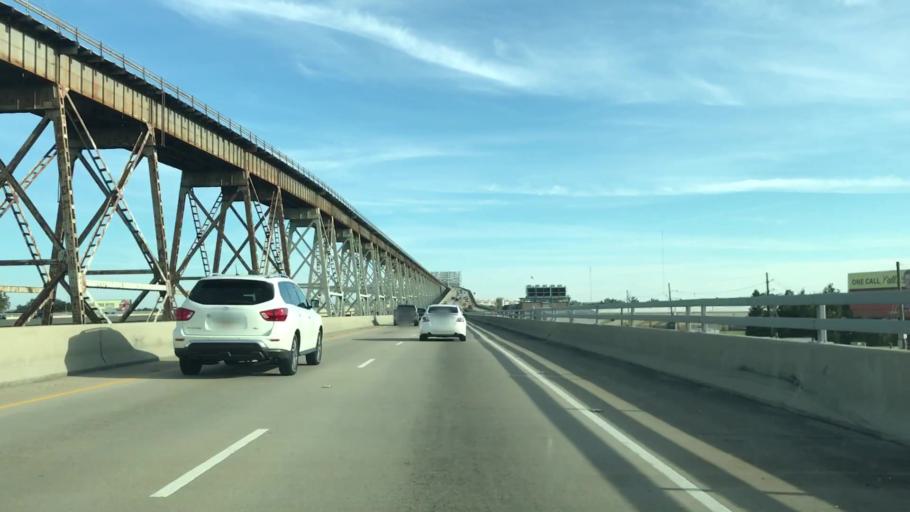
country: US
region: Louisiana
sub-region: Jefferson Parish
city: Elmwood
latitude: 29.9532
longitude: -90.1796
